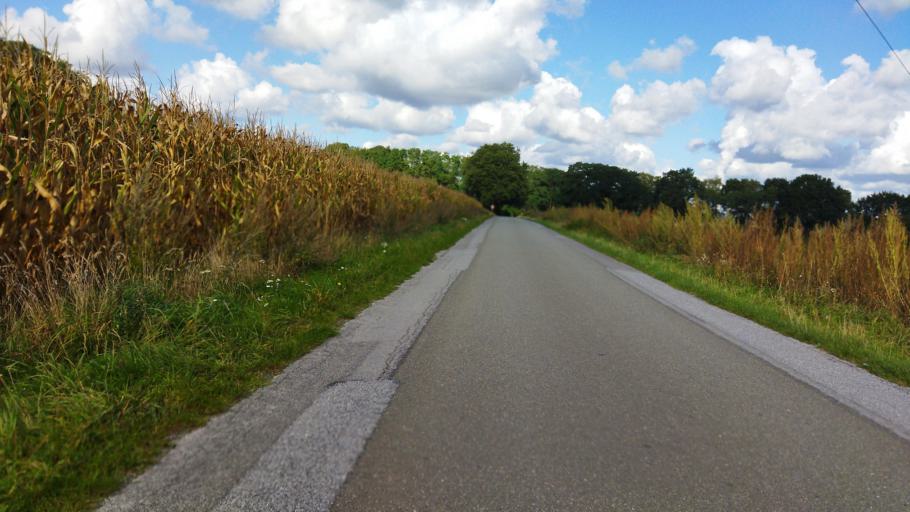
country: DE
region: Lower Saxony
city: Emsburen
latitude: 52.3907
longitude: 7.3257
